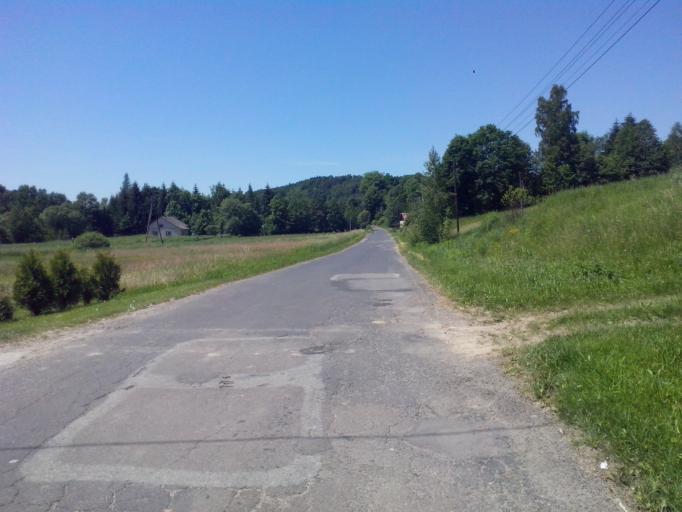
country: PL
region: Subcarpathian Voivodeship
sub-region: Powiat krosnienski
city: Leki
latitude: 49.8061
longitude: 21.6904
